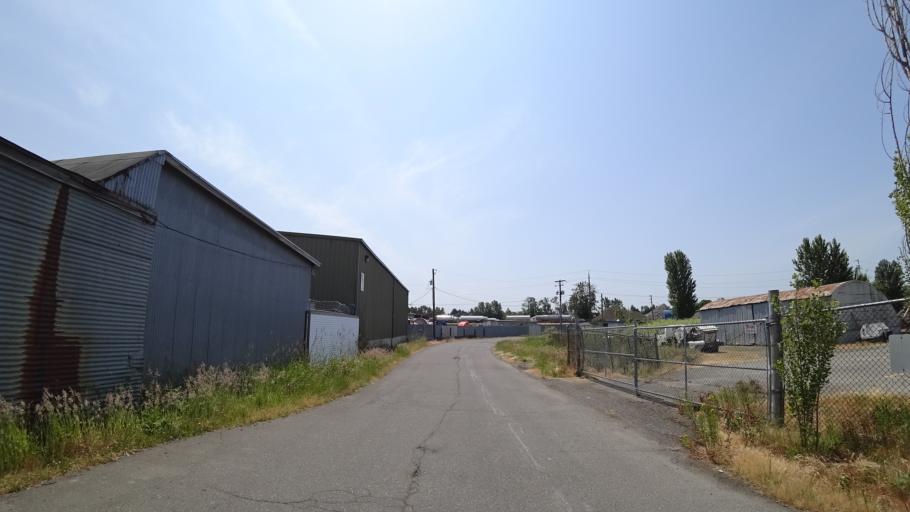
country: US
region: Washington
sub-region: Clark County
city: Vancouver
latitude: 45.5888
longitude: -122.6690
